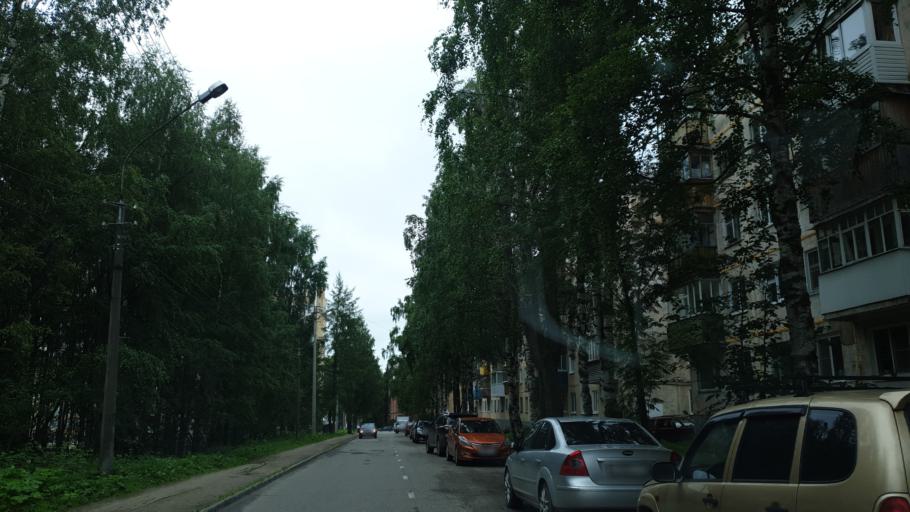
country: RU
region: Komi Republic
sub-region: Syktyvdinskiy Rayon
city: Syktyvkar
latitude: 61.6614
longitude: 50.8238
